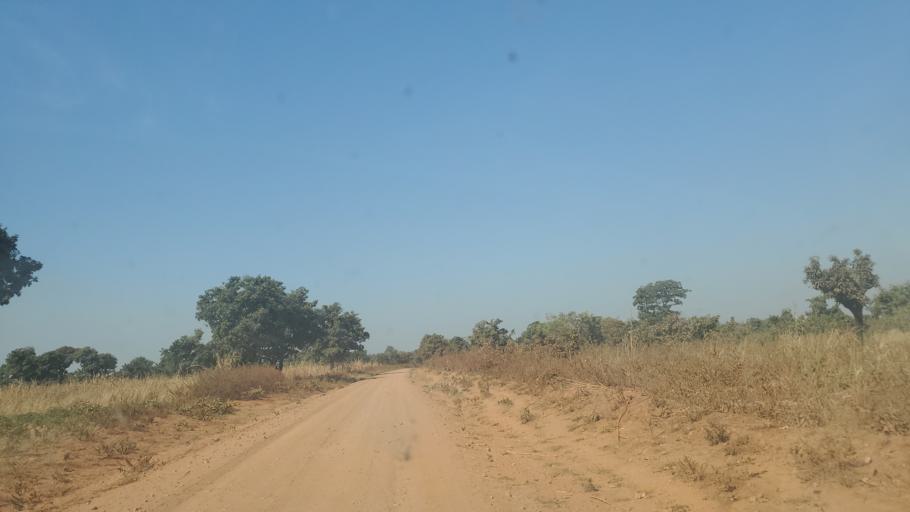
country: NG
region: Niger
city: Badeggi
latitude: 9.1204
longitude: 6.1928
